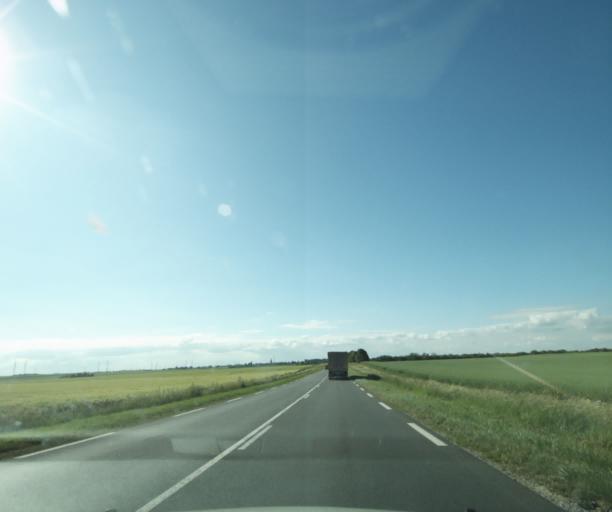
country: FR
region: Centre
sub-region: Departement d'Eure-et-Loir
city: Janville
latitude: 48.2499
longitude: 1.7692
